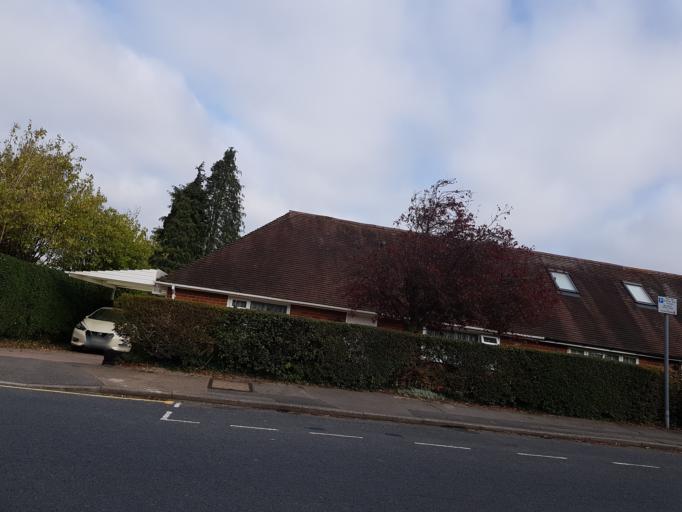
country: GB
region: England
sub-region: Surrey
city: Guildford
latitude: 51.2331
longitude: -0.5947
